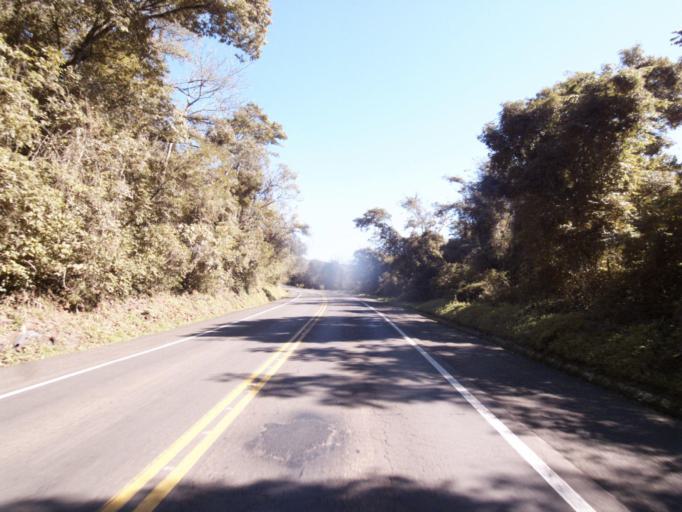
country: BR
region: Rio Grande do Sul
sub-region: Frederico Westphalen
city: Frederico Westphalen
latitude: -26.8227
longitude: -53.3885
